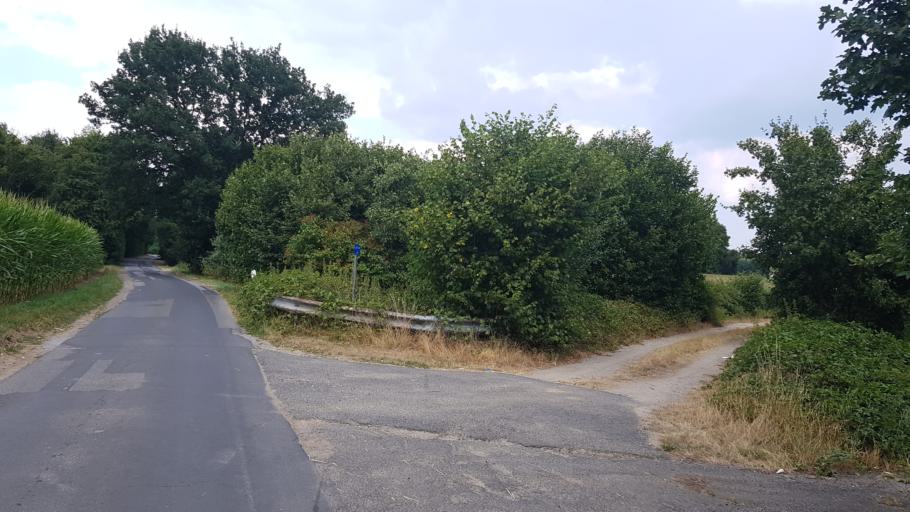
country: DE
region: North Rhine-Westphalia
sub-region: Regierungsbezirk Dusseldorf
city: Kamp-Lintfort
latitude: 51.4642
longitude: 6.5706
